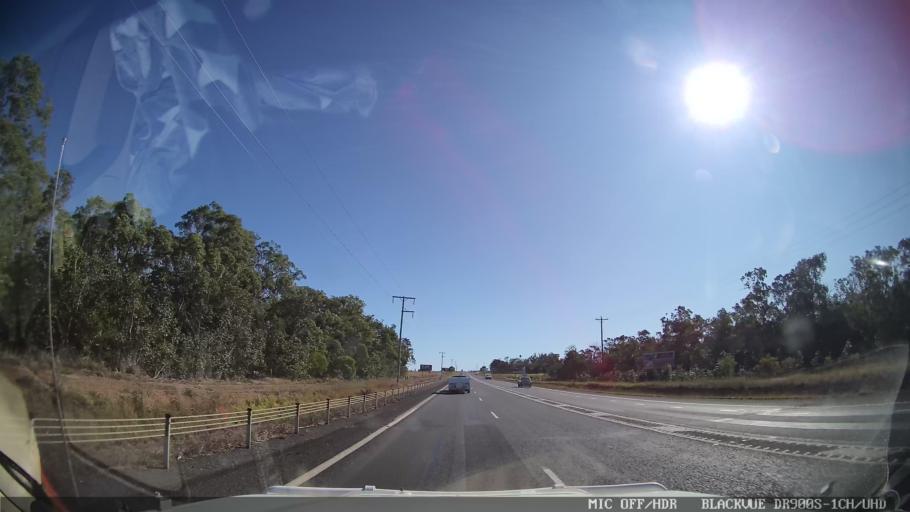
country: AU
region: Queensland
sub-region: Bundaberg
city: Childers
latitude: -25.2484
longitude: 152.3336
